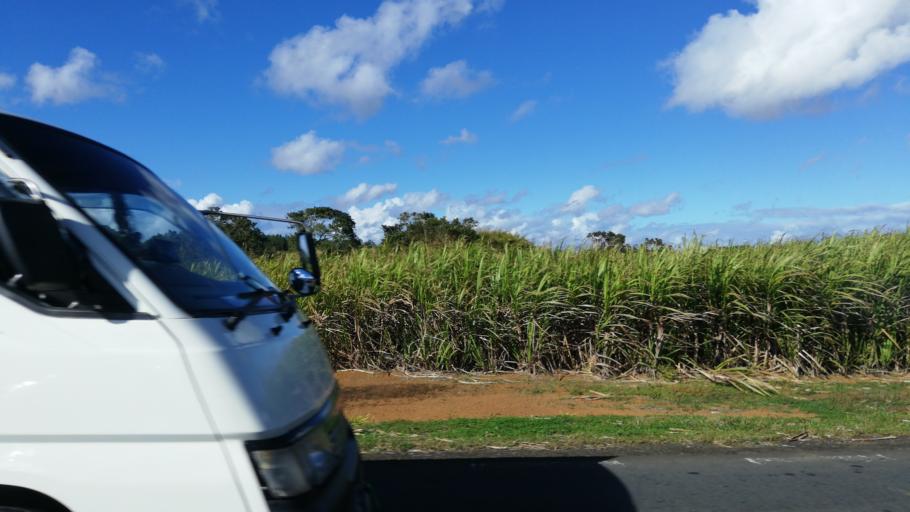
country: MU
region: Moka
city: La Dagotiere
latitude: -20.2322
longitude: 57.5602
